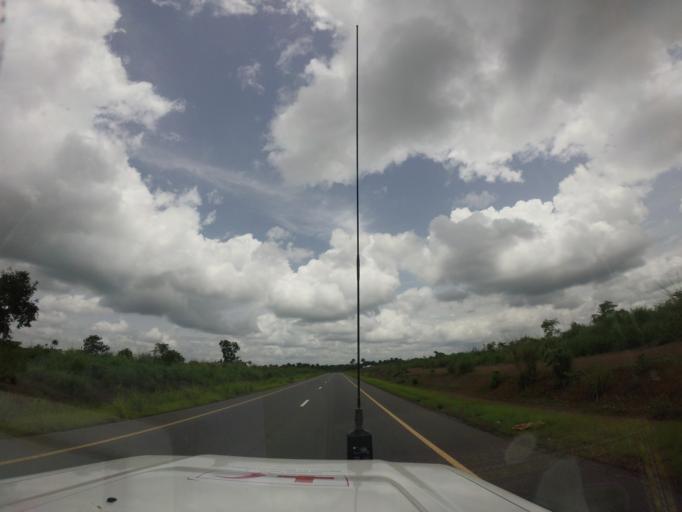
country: SL
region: Northern Province
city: Mange
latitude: 8.9818
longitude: -12.8629
